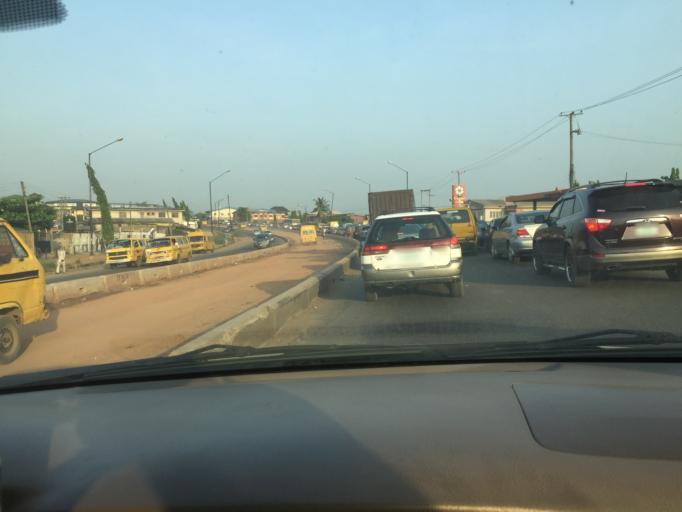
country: NG
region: Lagos
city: Agege
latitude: 6.6053
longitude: 3.3149
